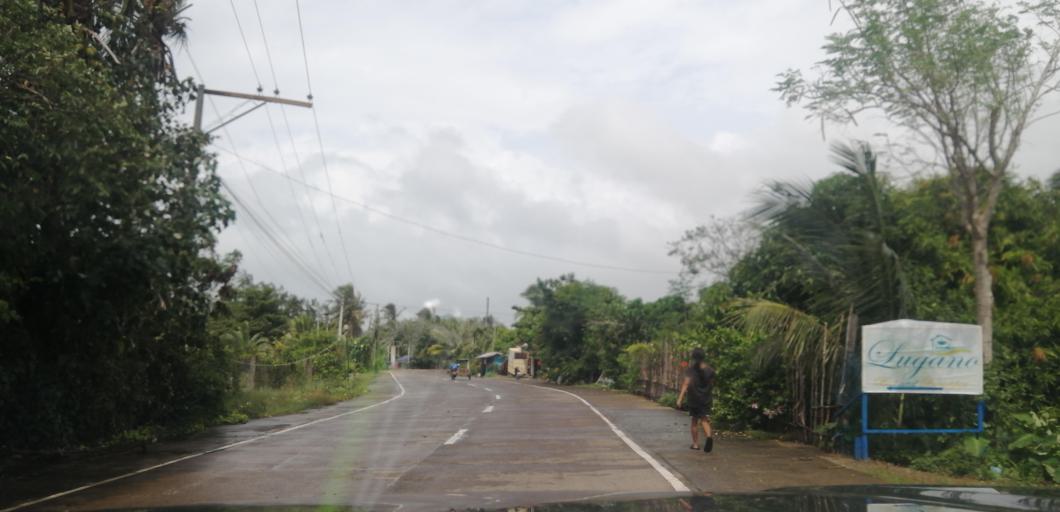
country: PH
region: Cagayan Valley
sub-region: Province of Cagayan
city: San Vicente
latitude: 18.5055
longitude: 122.1516
